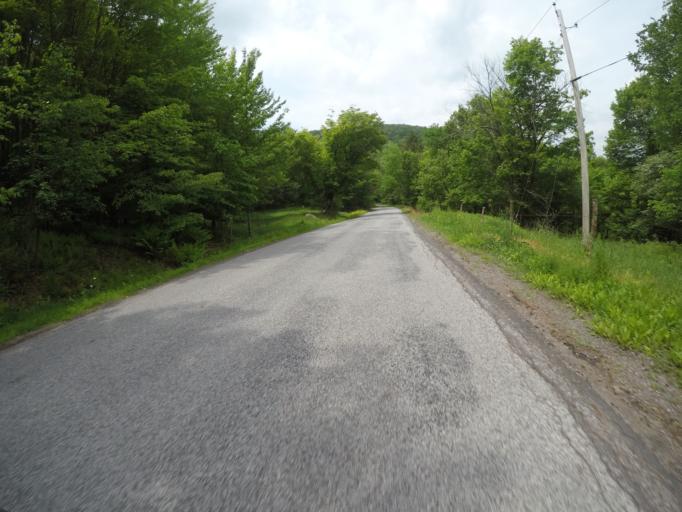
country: US
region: New York
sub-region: Delaware County
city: Stamford
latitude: 42.2595
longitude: -74.7209
